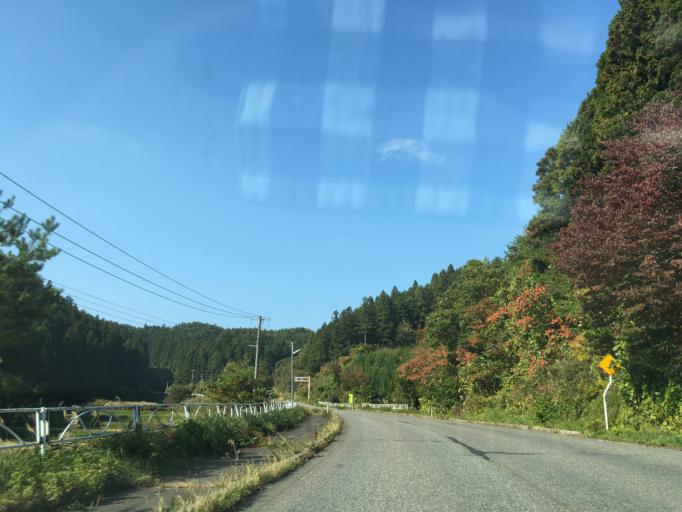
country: JP
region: Fukushima
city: Inawashiro
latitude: 37.3864
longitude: 140.1078
